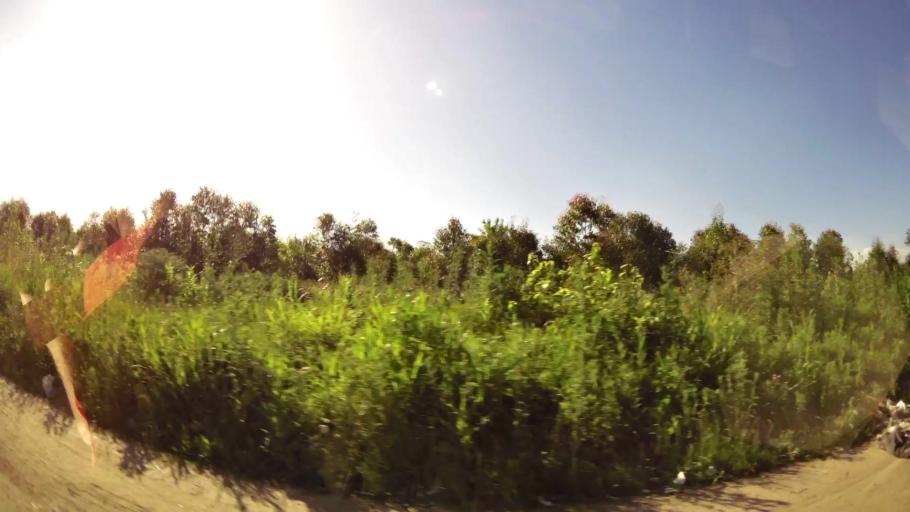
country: UY
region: Canelones
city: La Paz
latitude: -34.8097
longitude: -56.1654
